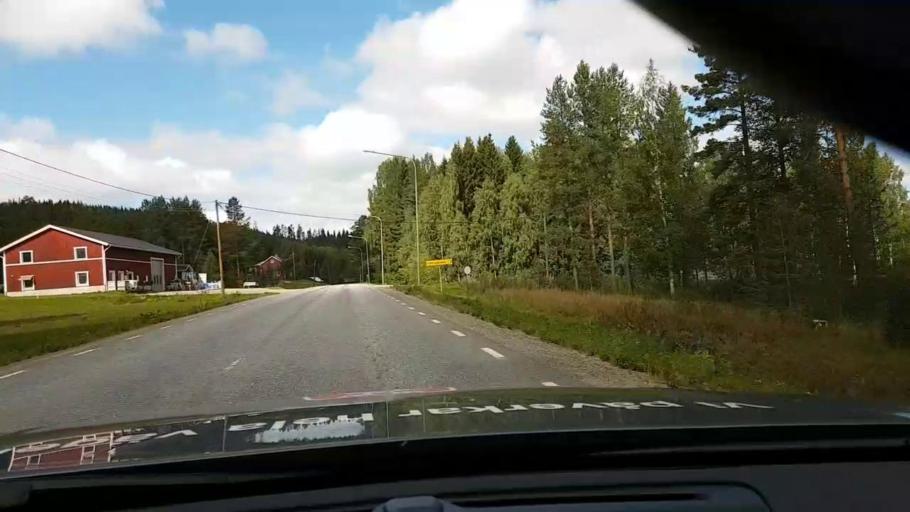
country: SE
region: Vaesternorrland
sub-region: OErnskoeldsviks Kommun
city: Bredbyn
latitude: 63.4894
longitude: 18.0830
